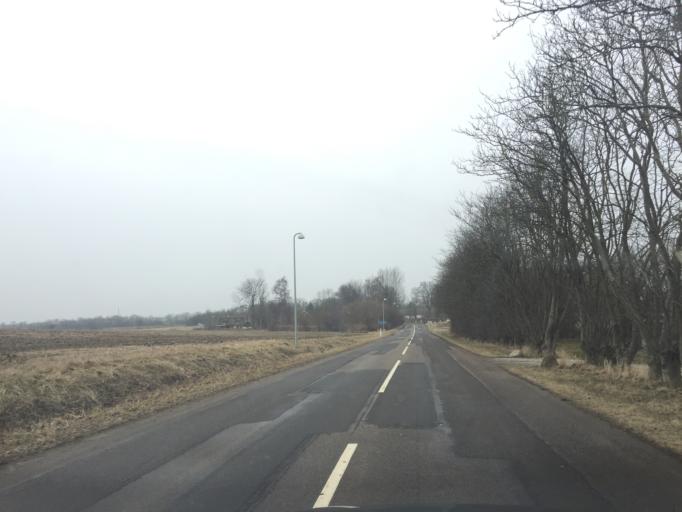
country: DK
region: Capital Region
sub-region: Hoje-Taastrup Kommune
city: Flong
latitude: 55.6409
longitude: 12.2228
